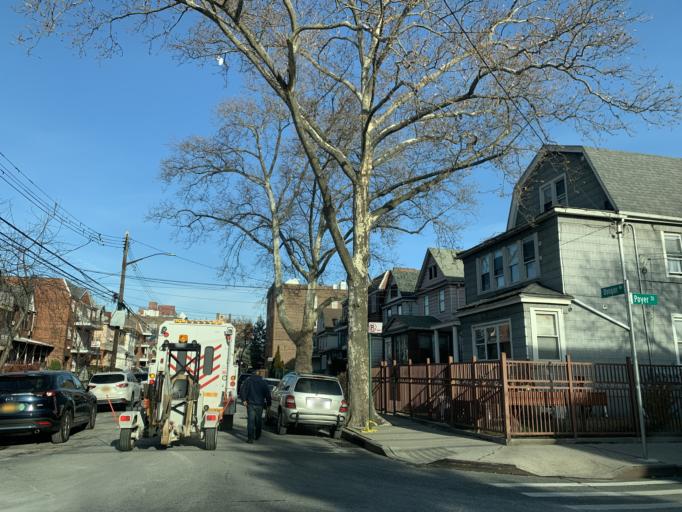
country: US
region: New York
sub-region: Queens County
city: Long Island City
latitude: 40.7394
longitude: -73.8808
